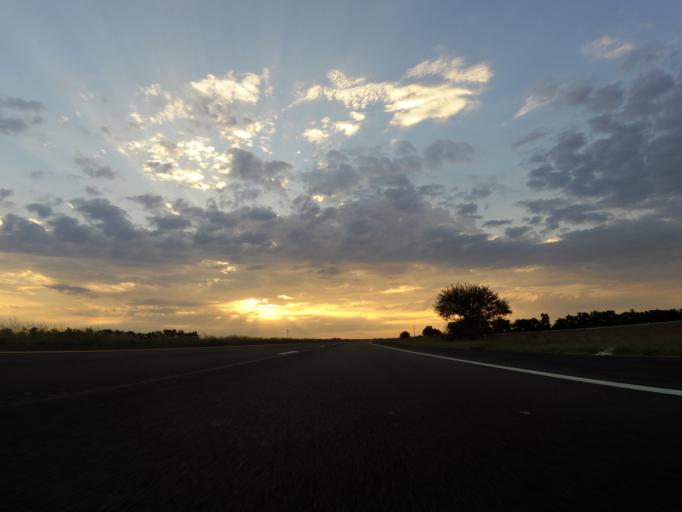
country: US
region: Kansas
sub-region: Sedgwick County
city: Colwich
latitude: 37.8755
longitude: -97.6366
